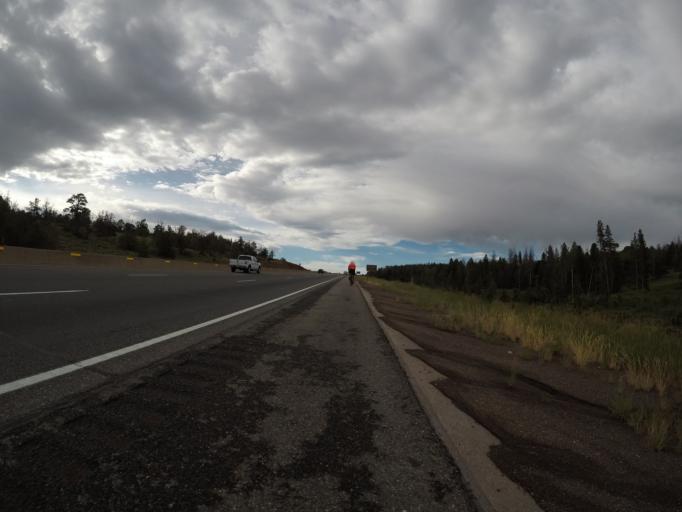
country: US
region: Wyoming
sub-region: Albany County
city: Laramie
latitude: 41.2510
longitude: -105.4450
